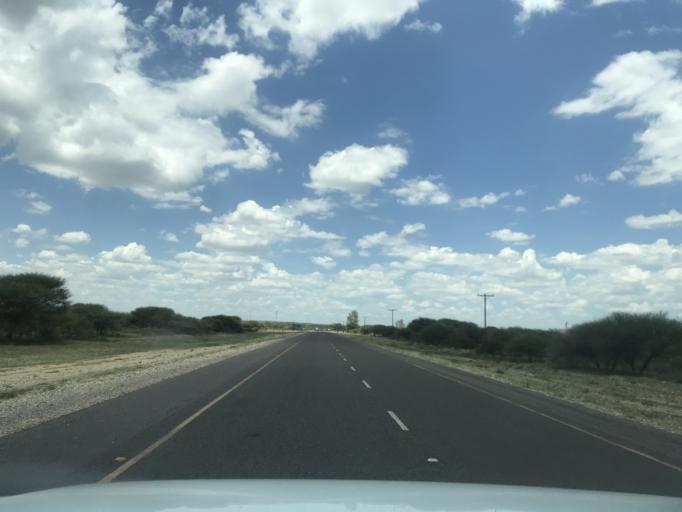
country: BW
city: Mabuli
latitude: -25.7312
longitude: 25.1110
